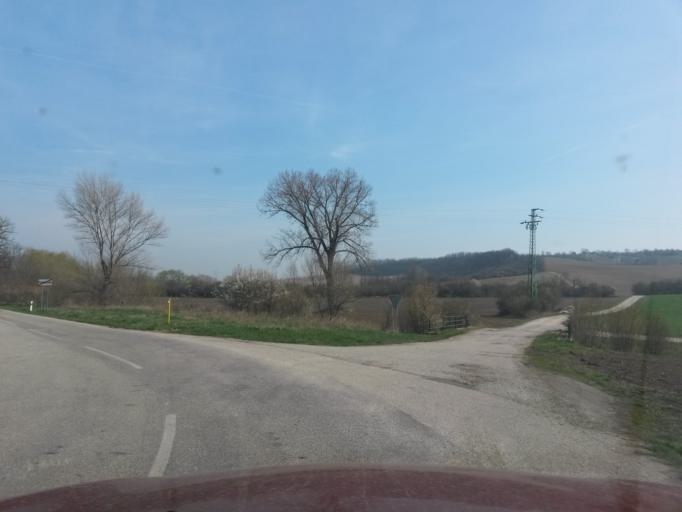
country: SK
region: Nitriansky
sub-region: Okres Nitra
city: Vrable
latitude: 48.1080
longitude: 18.3558
